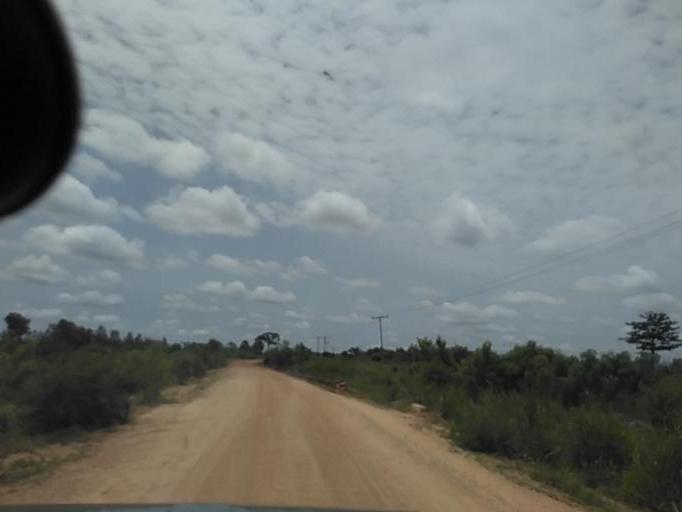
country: GH
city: Akropong
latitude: 6.0296
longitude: 0.3595
